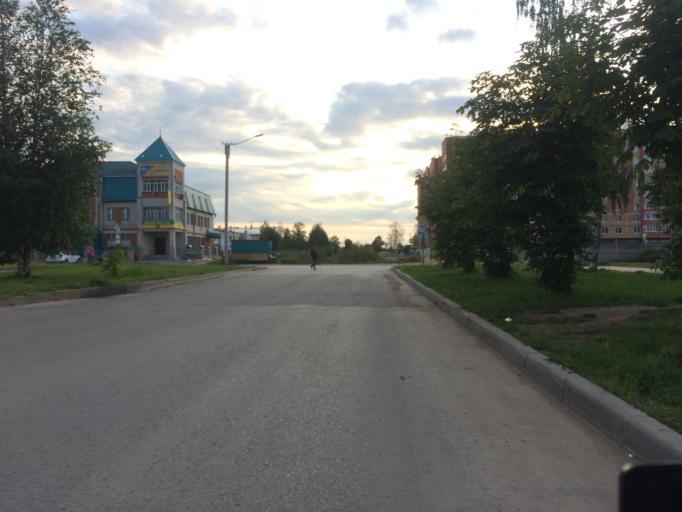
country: RU
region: Mariy-El
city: Medvedevo
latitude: 56.6447
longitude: 47.8359
